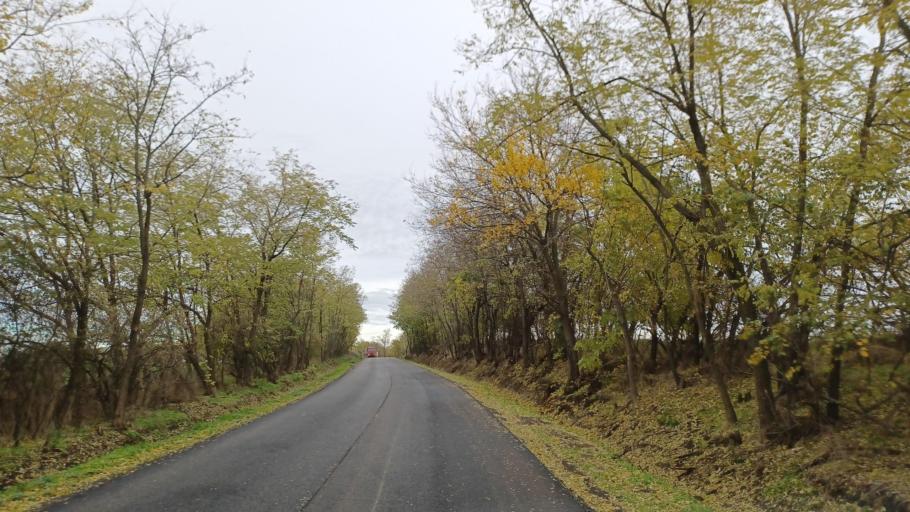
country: HU
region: Tolna
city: Tengelic
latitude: 46.5389
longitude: 18.7575
